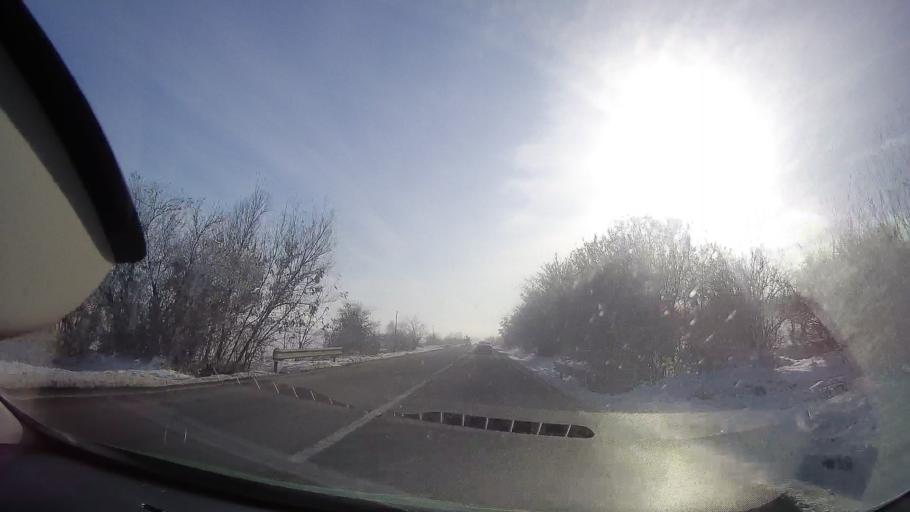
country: RO
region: Neamt
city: Bodesti
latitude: 47.0102
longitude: 26.4243
